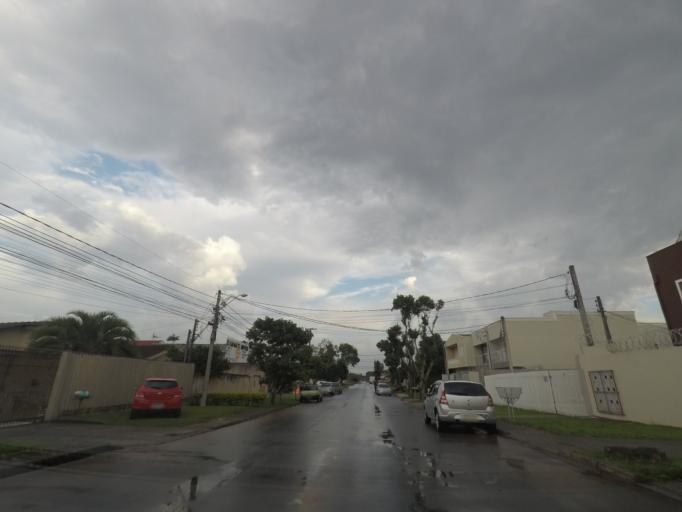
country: BR
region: Parana
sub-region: Sao Jose Dos Pinhais
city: Sao Jose dos Pinhais
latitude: -25.4874
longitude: -49.2499
